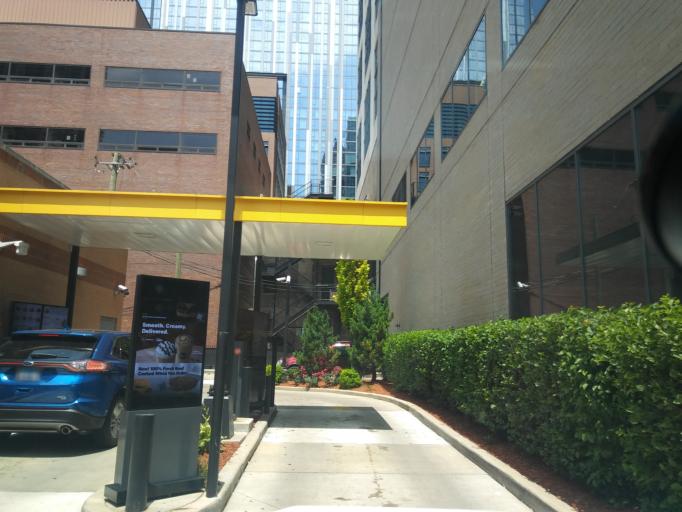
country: US
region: Illinois
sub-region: Cook County
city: Chicago
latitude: 41.8968
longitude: -87.6274
